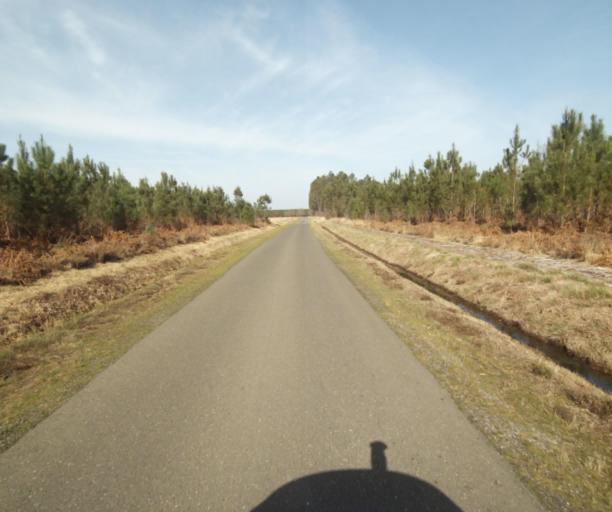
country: FR
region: Aquitaine
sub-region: Departement des Landes
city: Roquefort
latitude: 44.2134
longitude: -0.2038
